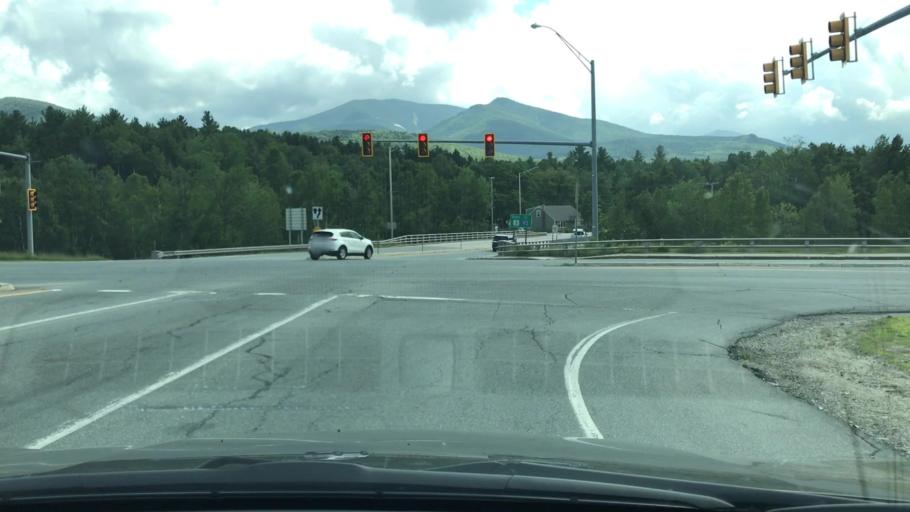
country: US
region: New Hampshire
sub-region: Grafton County
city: Deerfield
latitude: 44.2712
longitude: -71.5399
